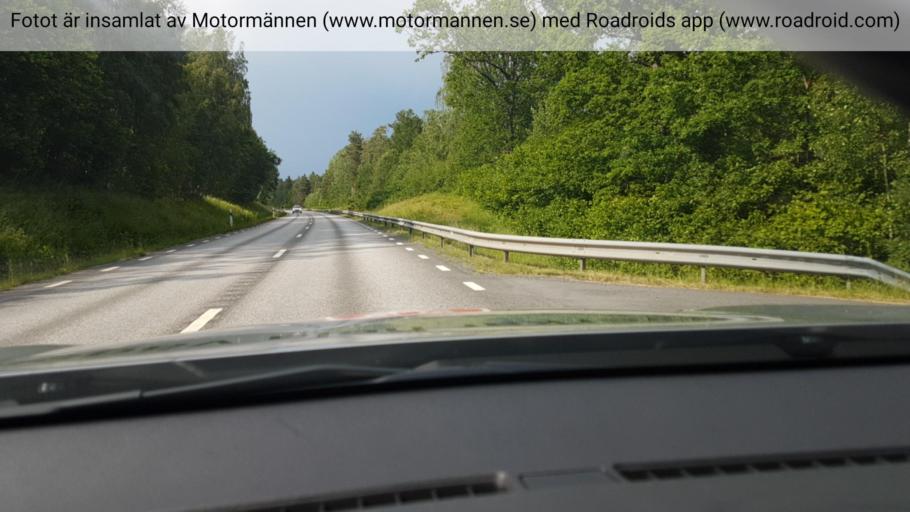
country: SE
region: Joenkoeping
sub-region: Habo Kommun
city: Habo
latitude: 58.0670
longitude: 14.1958
